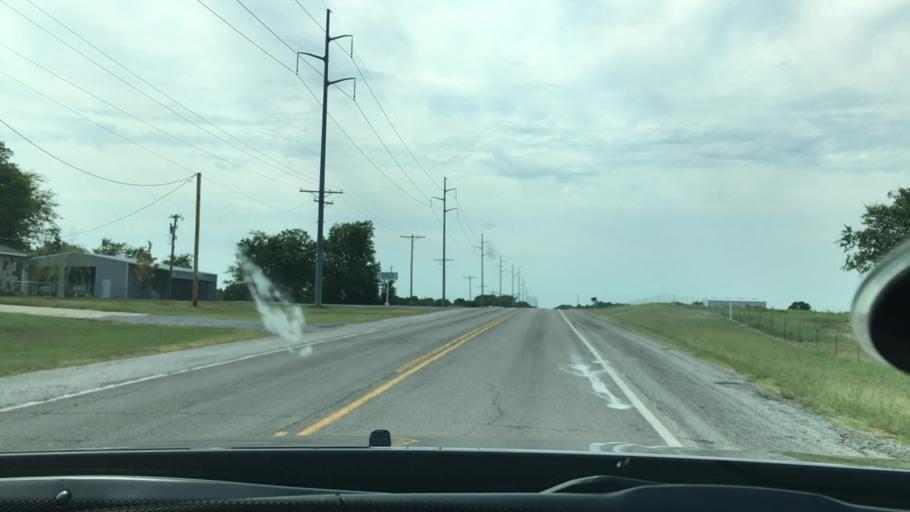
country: US
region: Oklahoma
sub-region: Carter County
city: Ardmore
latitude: 34.3258
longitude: -97.1430
